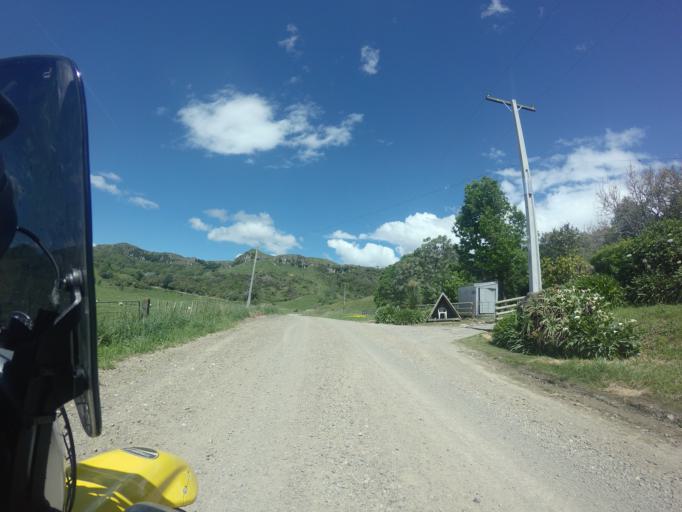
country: NZ
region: Hawke's Bay
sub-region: Wairoa District
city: Wairoa
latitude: -38.9904
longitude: 177.7100
